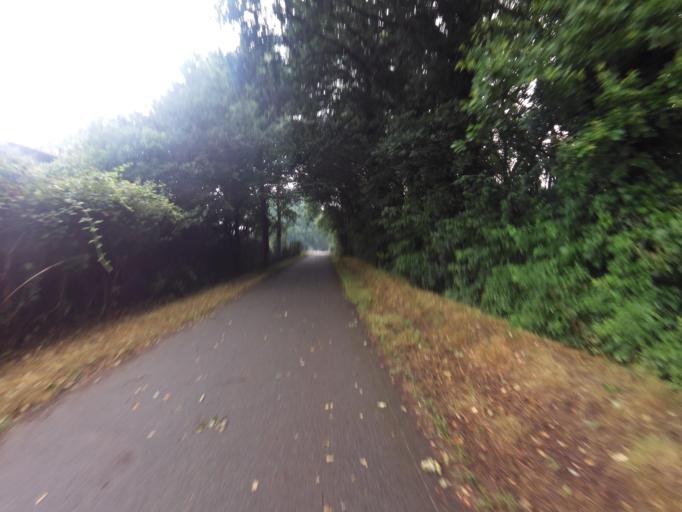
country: FR
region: Brittany
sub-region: Departement du Morbihan
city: Guillac
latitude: 47.8663
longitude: -2.4384
